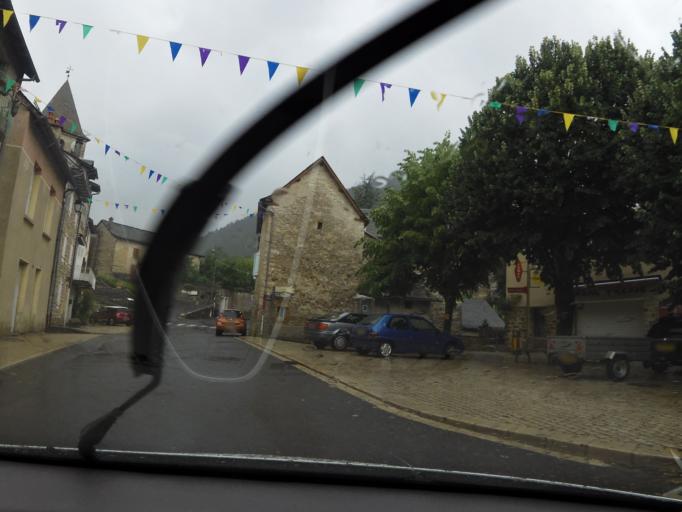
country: FR
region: Languedoc-Roussillon
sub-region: Departement de la Lozere
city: Chanac
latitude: 44.4652
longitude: 3.3444
